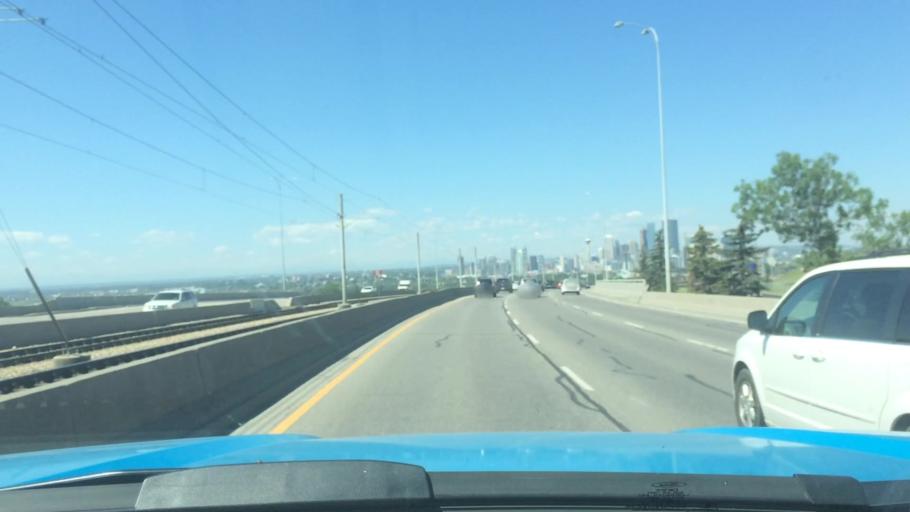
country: CA
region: Alberta
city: Calgary
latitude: 51.0466
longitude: -114.0010
